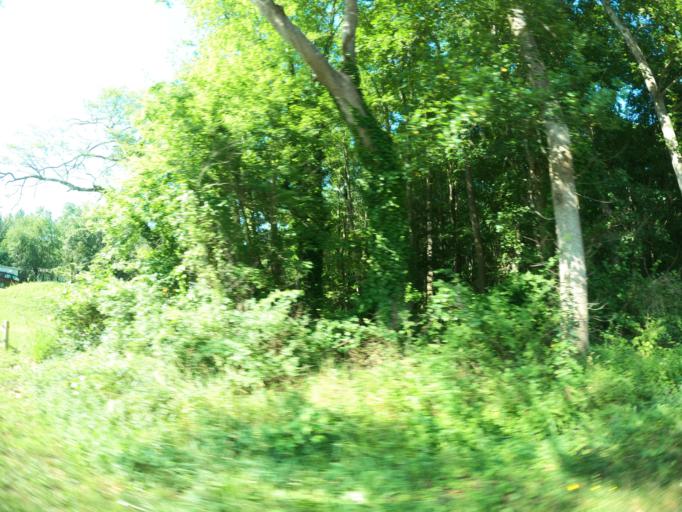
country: US
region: Delaware
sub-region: Sussex County
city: Ocean View
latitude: 38.4929
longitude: -75.1281
